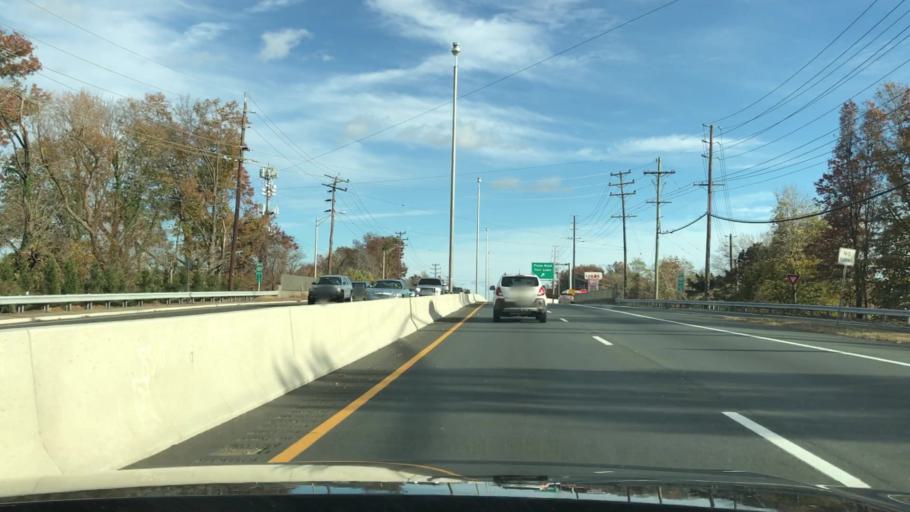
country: US
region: New Jersey
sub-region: Bergen County
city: Fair Lawn
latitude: 40.9344
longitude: -74.1208
